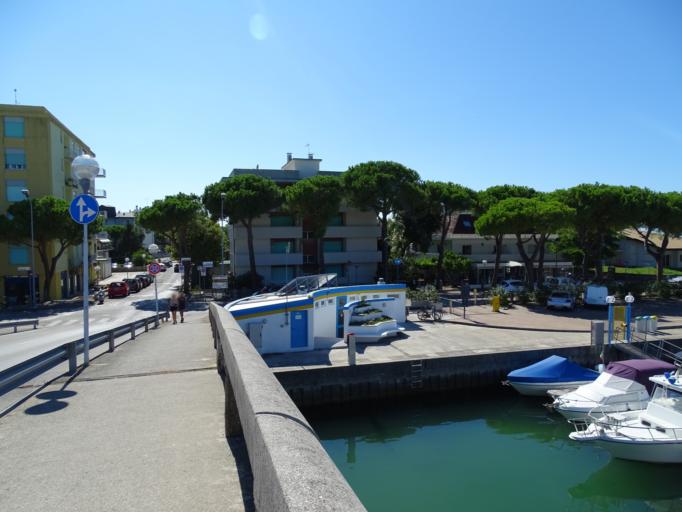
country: IT
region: Friuli Venezia Giulia
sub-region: Provincia di Udine
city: Lignano Sabbiadoro
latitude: 45.6948
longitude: 13.1453
